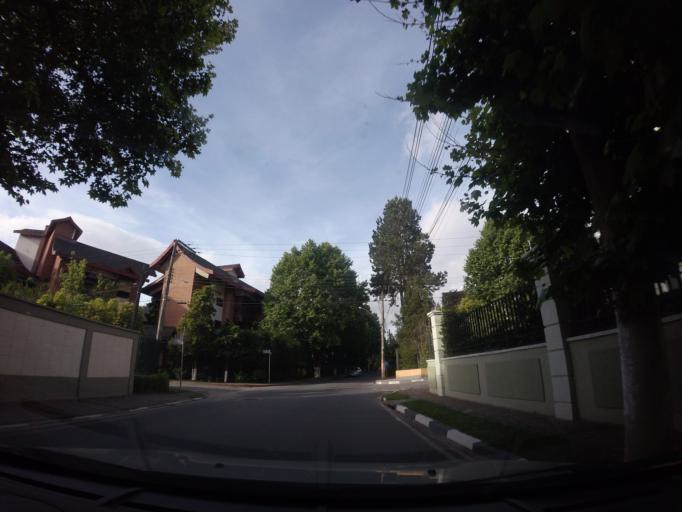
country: BR
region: Sao Paulo
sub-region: Campos Do Jordao
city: Campos do Jordao
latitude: -22.7285
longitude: -45.5695
